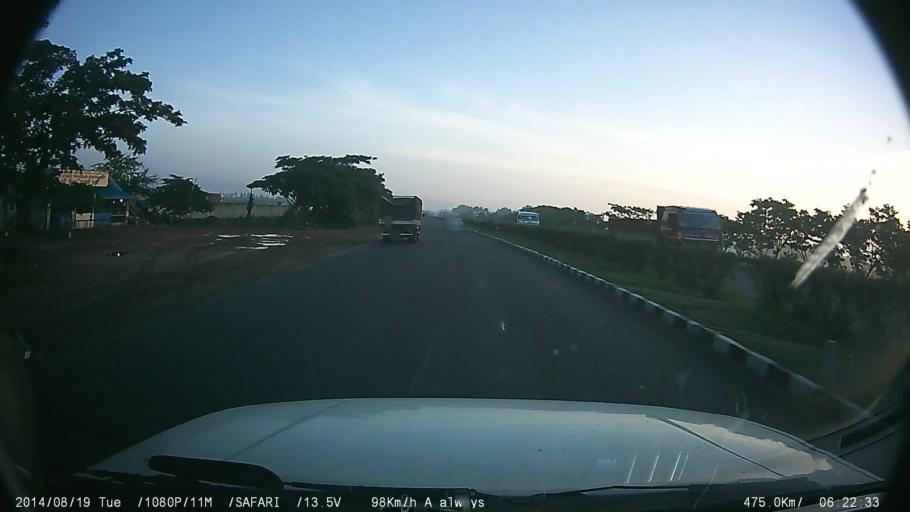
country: IN
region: Tamil Nadu
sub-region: Dharmapuri
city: Dharmapuri
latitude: 12.0264
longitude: 78.1004
